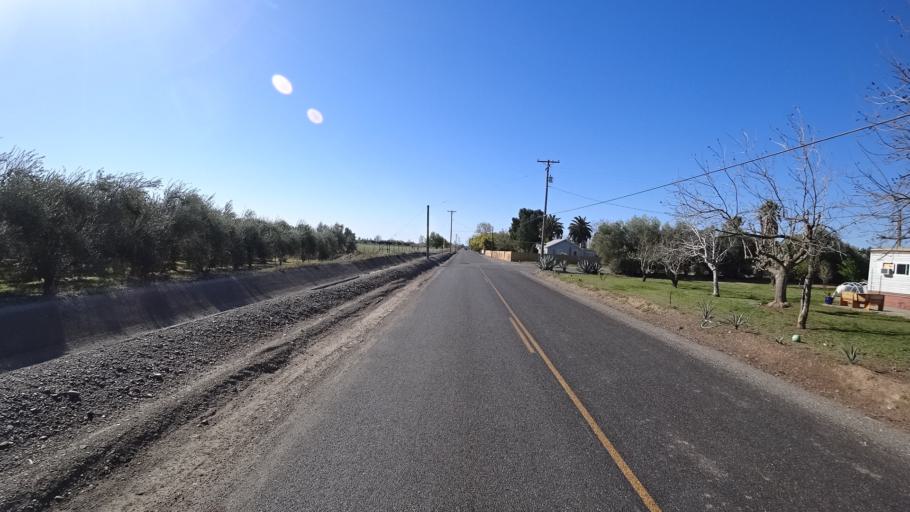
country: US
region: California
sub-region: Glenn County
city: Orland
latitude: 39.7372
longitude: -122.2157
